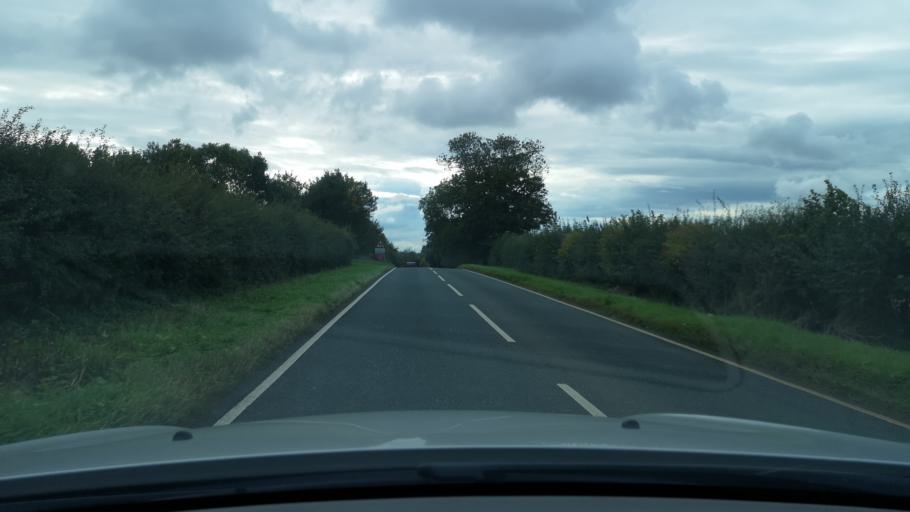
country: GB
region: England
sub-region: East Riding of Yorkshire
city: Hotham
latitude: 53.7875
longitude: -0.6309
